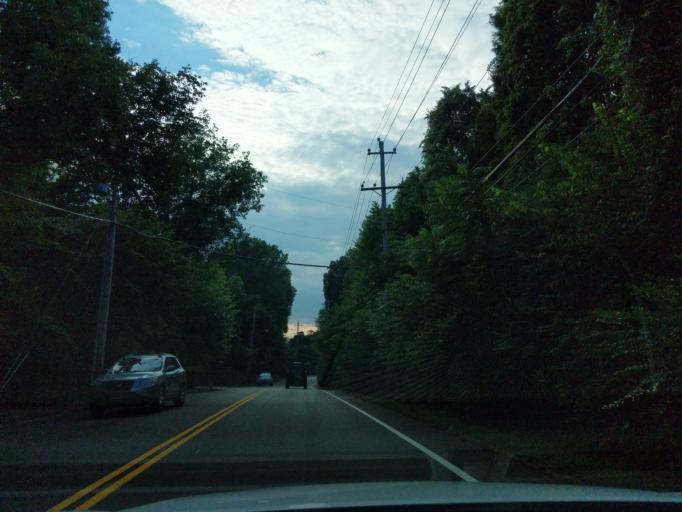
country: US
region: Tennessee
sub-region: Shelby County
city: Germantown
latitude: 35.0734
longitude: -89.7894
